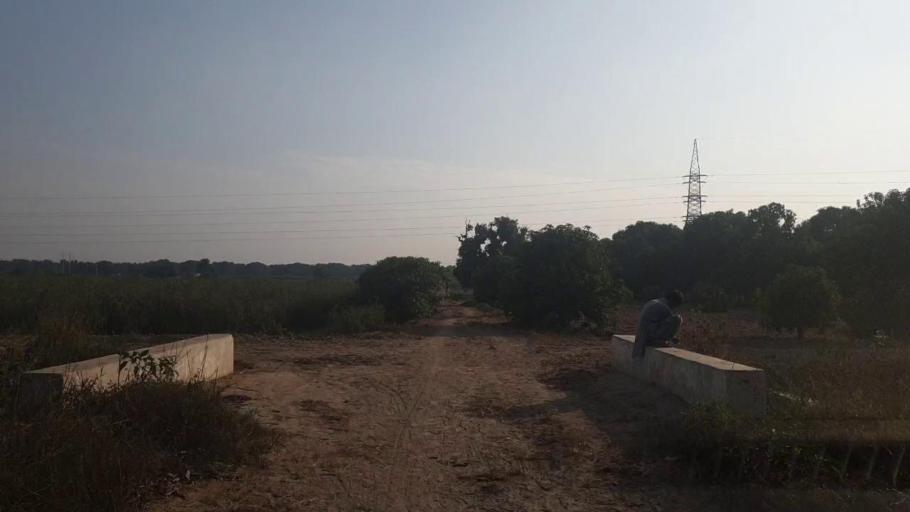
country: PK
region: Sindh
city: Tando Jam
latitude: 25.4281
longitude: 68.4620
